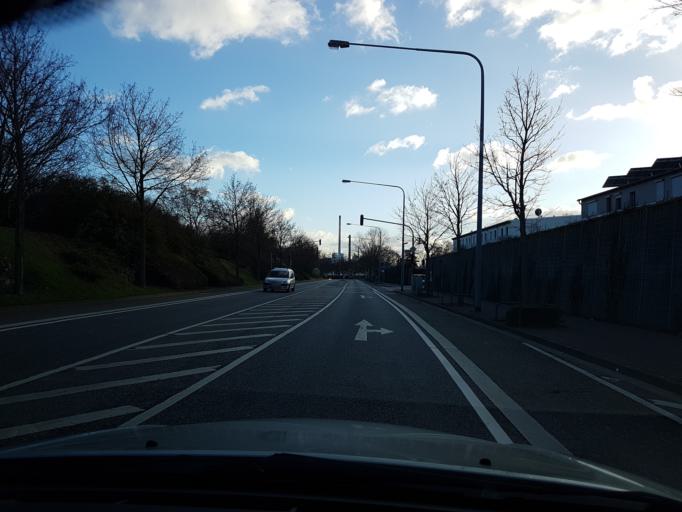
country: DE
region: Hesse
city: Sulzbach
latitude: 50.1050
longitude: 8.5287
